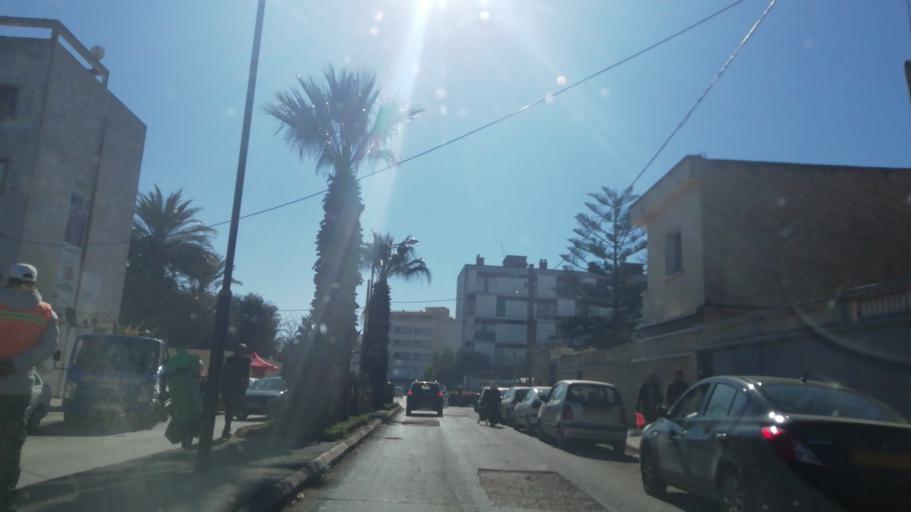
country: DZ
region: Oran
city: Es Senia
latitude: 35.6510
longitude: -0.6216
